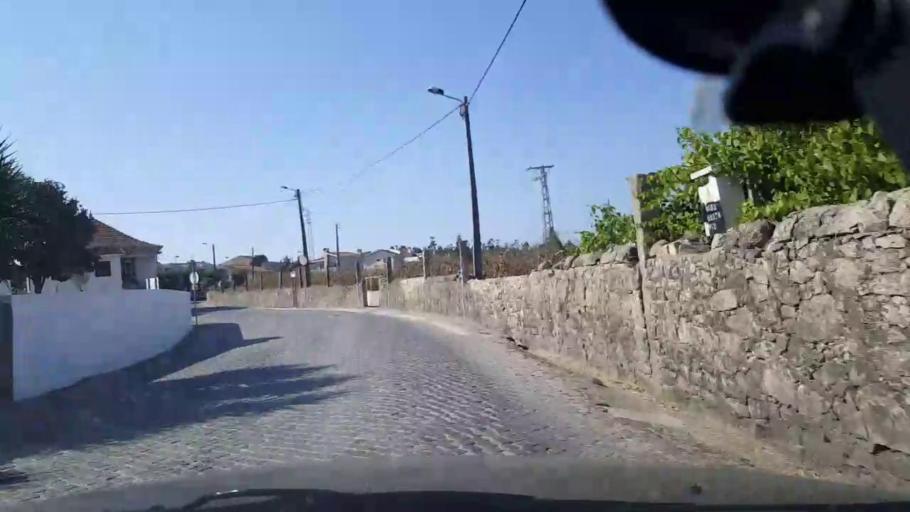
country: PT
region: Porto
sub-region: Vila do Conde
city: Arvore
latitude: 41.3811
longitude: -8.6811
